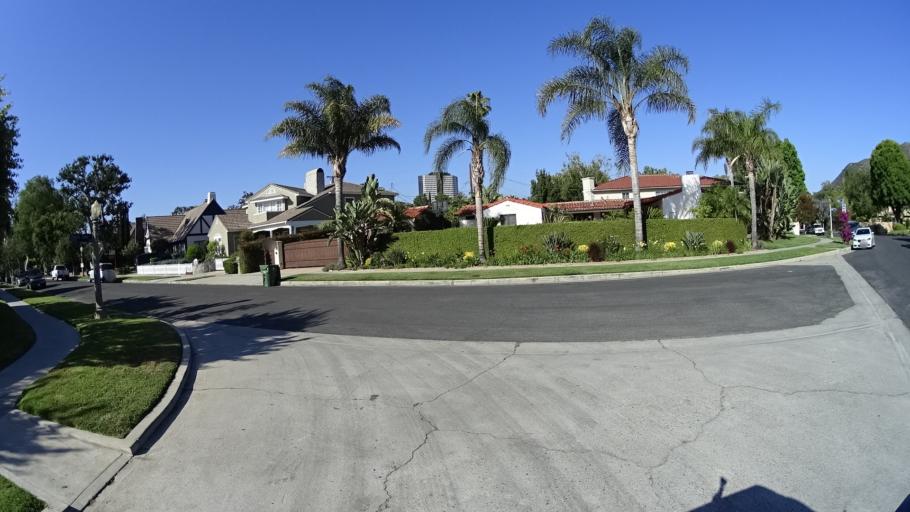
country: US
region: California
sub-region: Los Angeles County
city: Universal City
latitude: 34.1485
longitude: -118.3489
